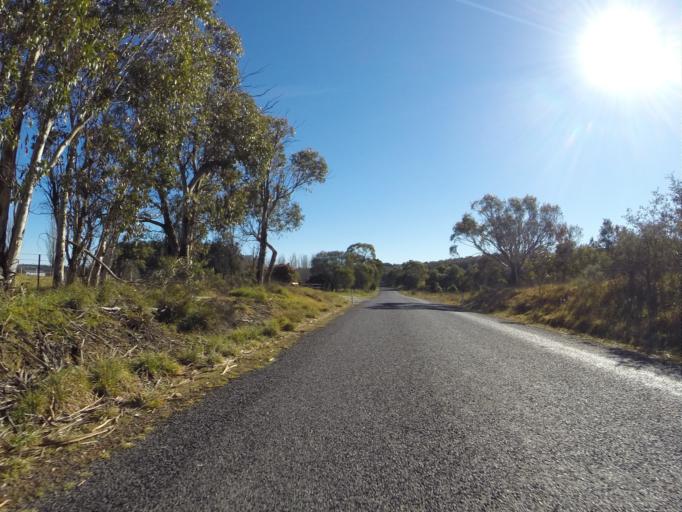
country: AU
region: New South Wales
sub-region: Oberon
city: Oberon
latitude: -33.6674
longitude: 149.8570
